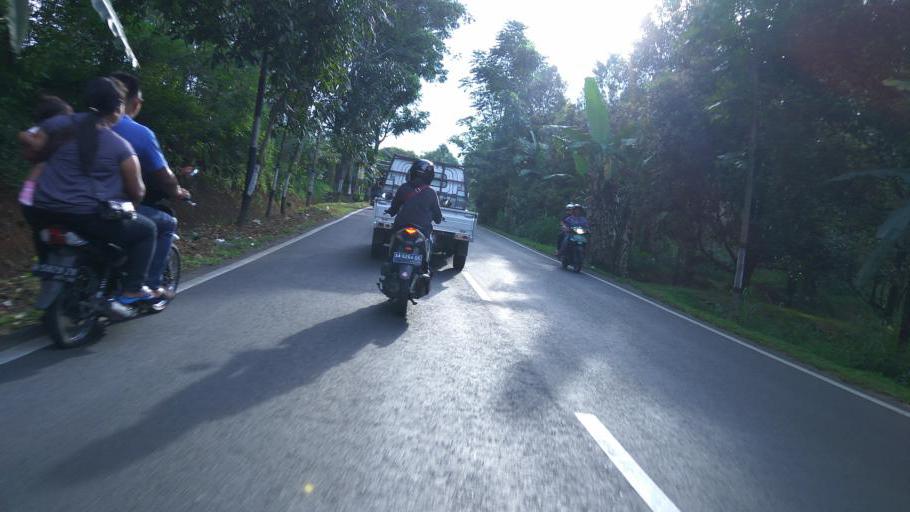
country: ID
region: Central Java
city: Salatiga
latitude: -7.3682
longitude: 110.4580
